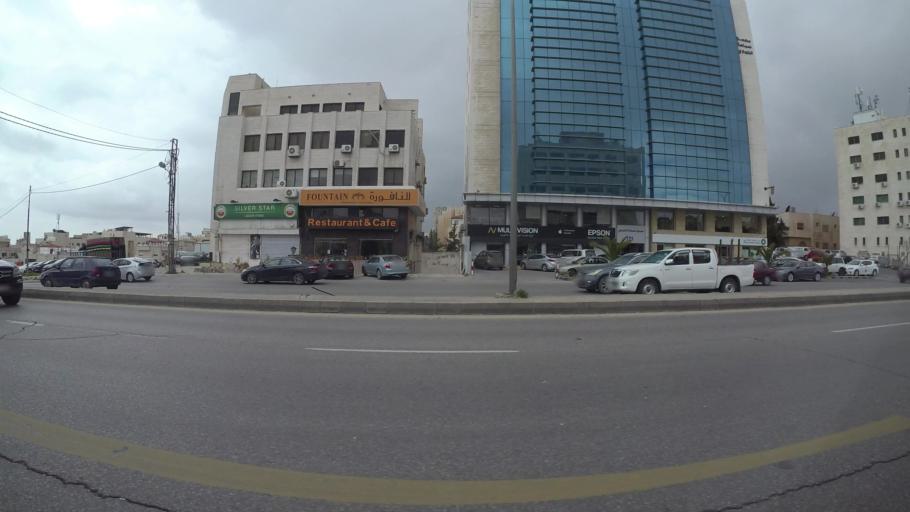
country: JO
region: Amman
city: Al Jubayhah
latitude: 31.9768
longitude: 35.8657
